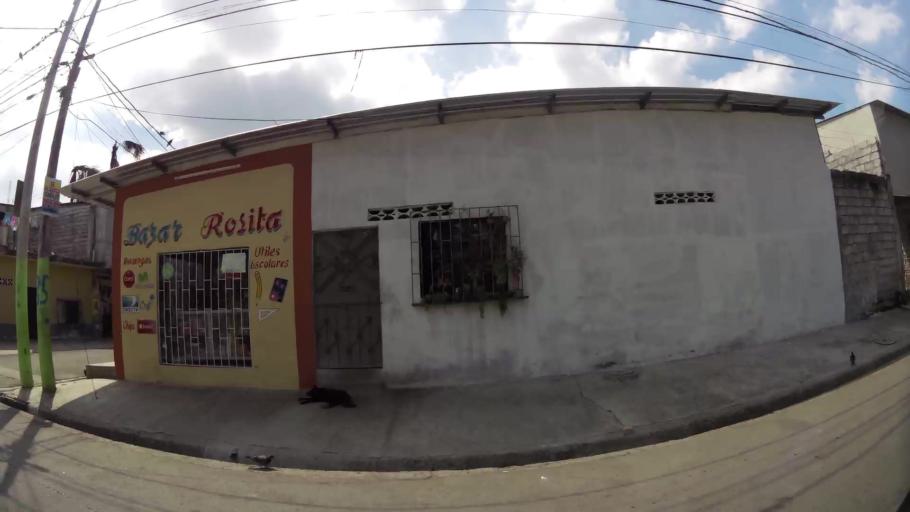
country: EC
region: Guayas
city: Santa Lucia
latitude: -2.1366
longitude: -79.9403
